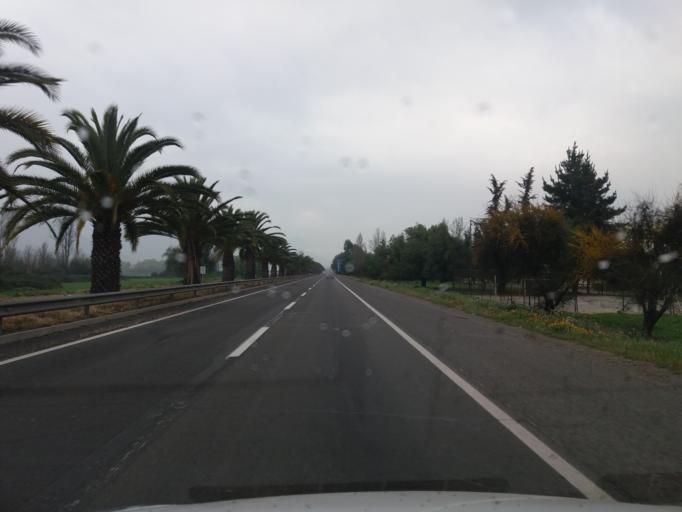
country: CL
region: Valparaiso
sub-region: Provincia de Quillota
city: Hacienda La Calera
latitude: -32.7807
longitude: -71.1774
